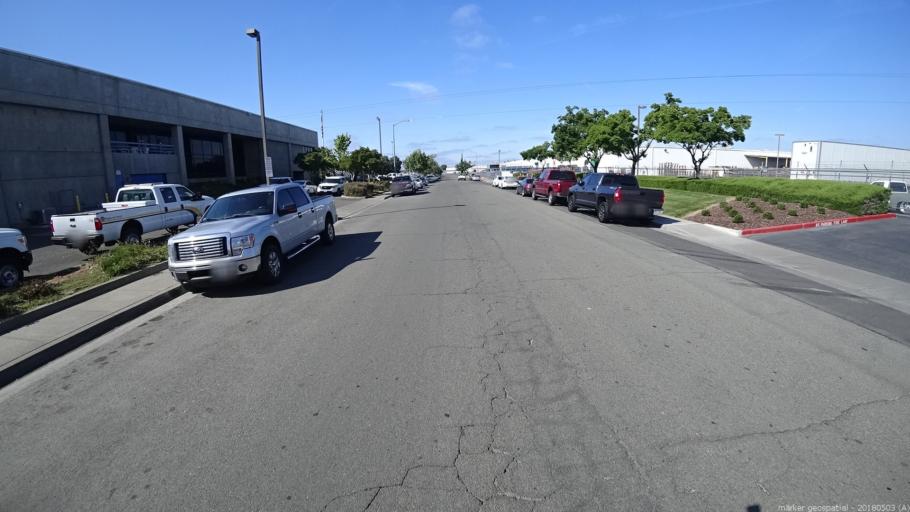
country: US
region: California
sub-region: Sacramento County
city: Arden-Arcade
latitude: 38.6166
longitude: -121.4312
